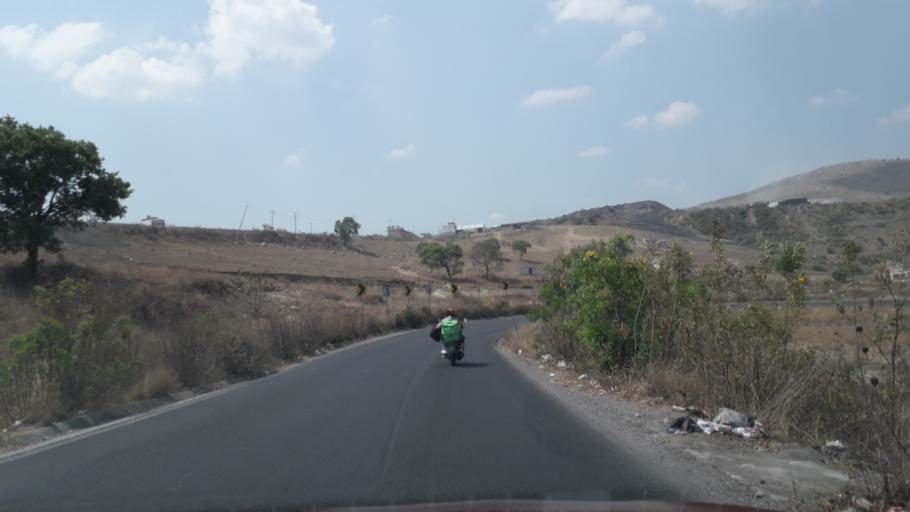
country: MX
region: Puebla
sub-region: Puebla
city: El Capulo (La Quebradora)
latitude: 18.9442
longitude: -98.2697
